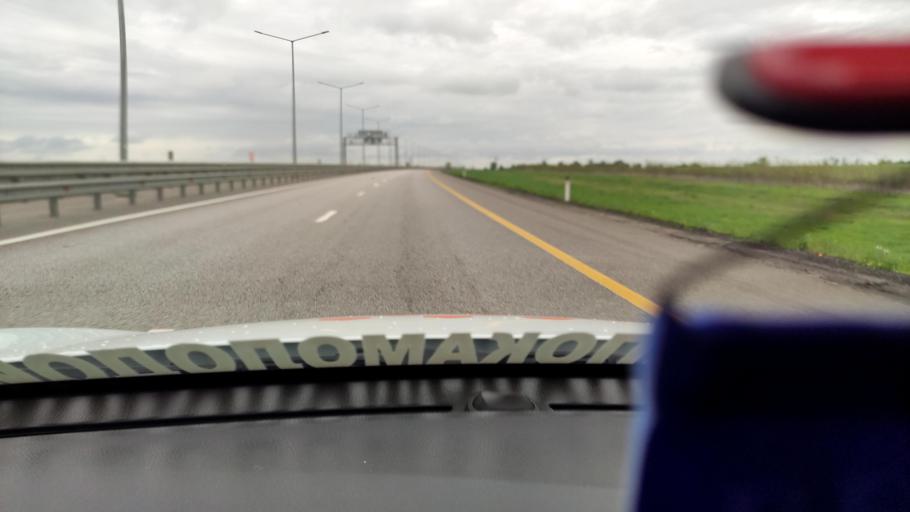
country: RU
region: Voronezj
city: Novaya Usman'
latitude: 51.6014
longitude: 39.3427
